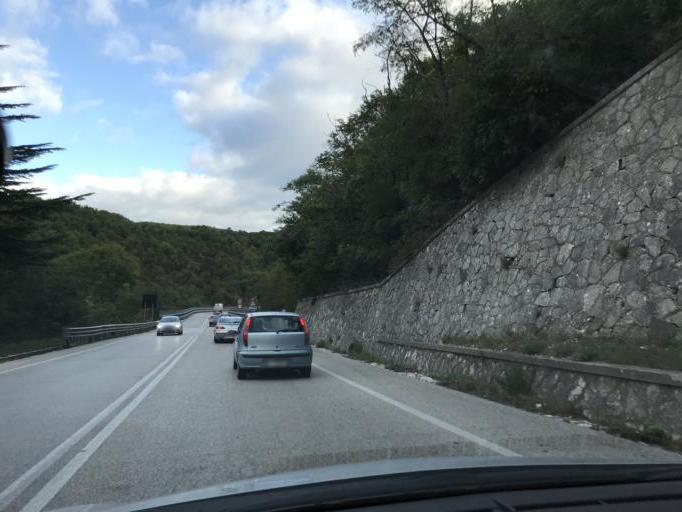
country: IT
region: Umbria
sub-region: Provincia di Terni
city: Ferentillo
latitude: 42.6744
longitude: 12.7266
